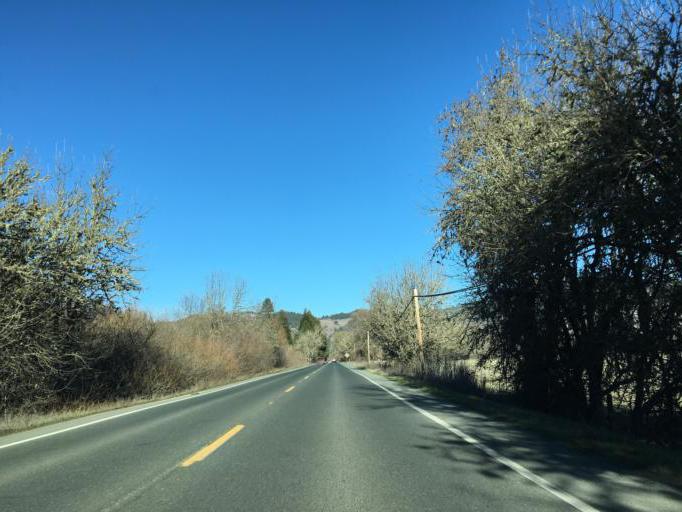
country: US
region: California
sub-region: Mendocino County
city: Brooktrails
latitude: 39.4435
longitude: -123.3532
